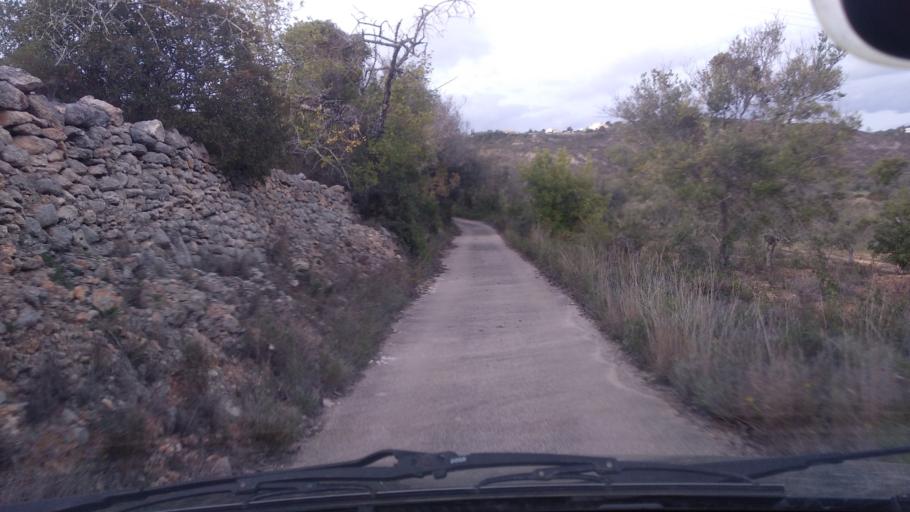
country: PT
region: Faro
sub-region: Sao Bras de Alportel
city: Sao Bras de Alportel
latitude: 37.1198
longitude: -7.9058
